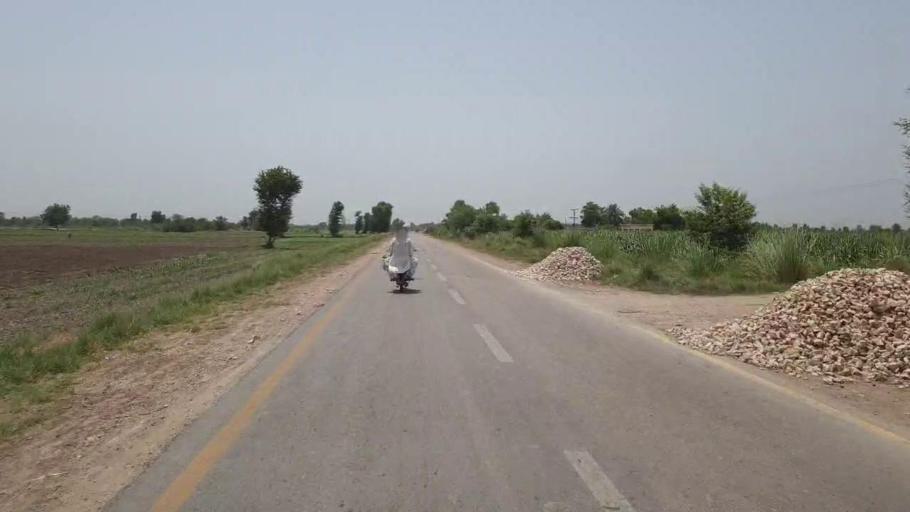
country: PK
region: Sindh
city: Moro
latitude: 26.6087
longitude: 68.0455
